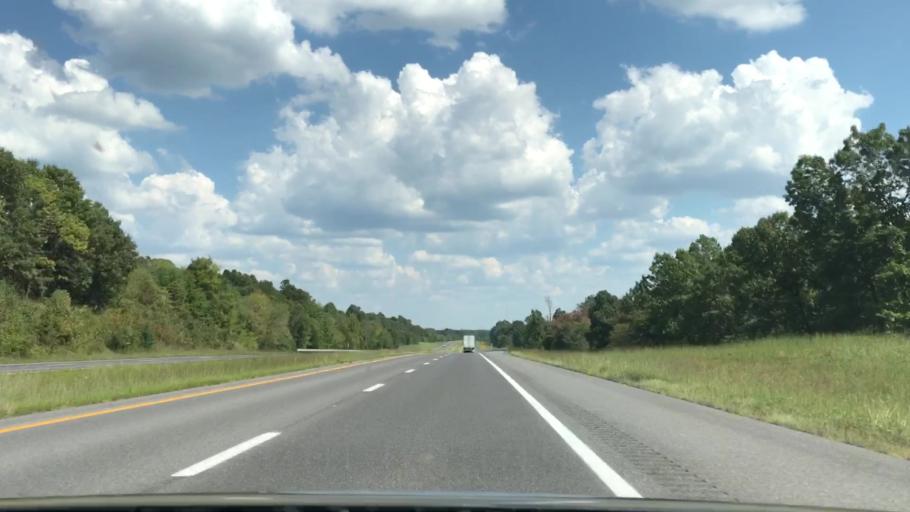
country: US
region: Kentucky
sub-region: Caldwell County
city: Princeton
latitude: 37.1078
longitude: -87.9800
